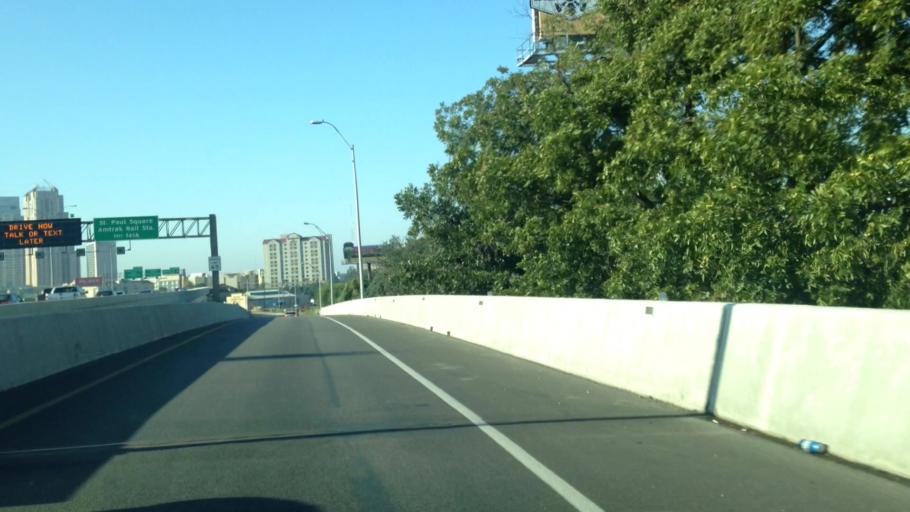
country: US
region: Texas
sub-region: Bexar County
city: San Antonio
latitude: 29.4319
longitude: -98.4799
